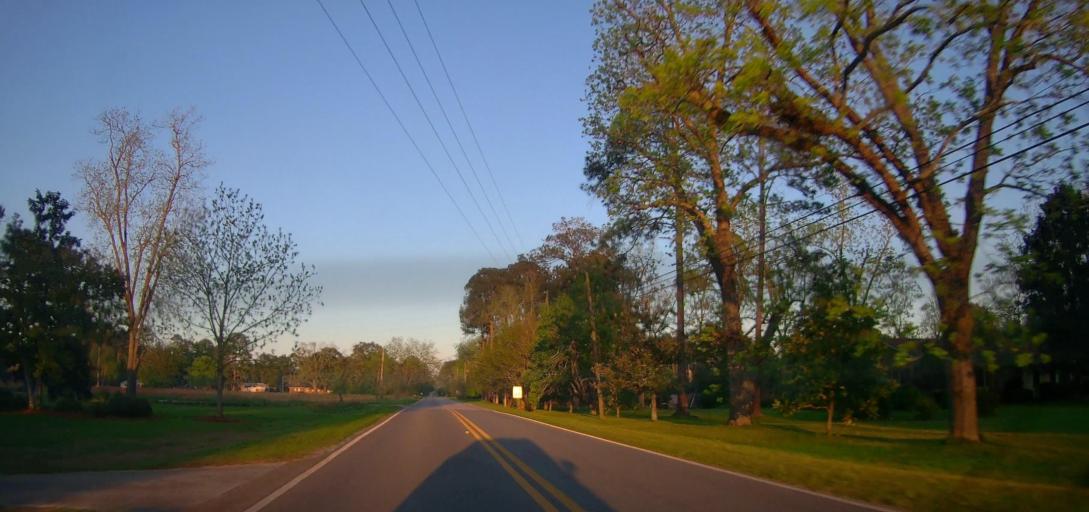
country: US
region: Georgia
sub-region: Ben Hill County
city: Fitzgerald
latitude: 31.7179
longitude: -83.2837
